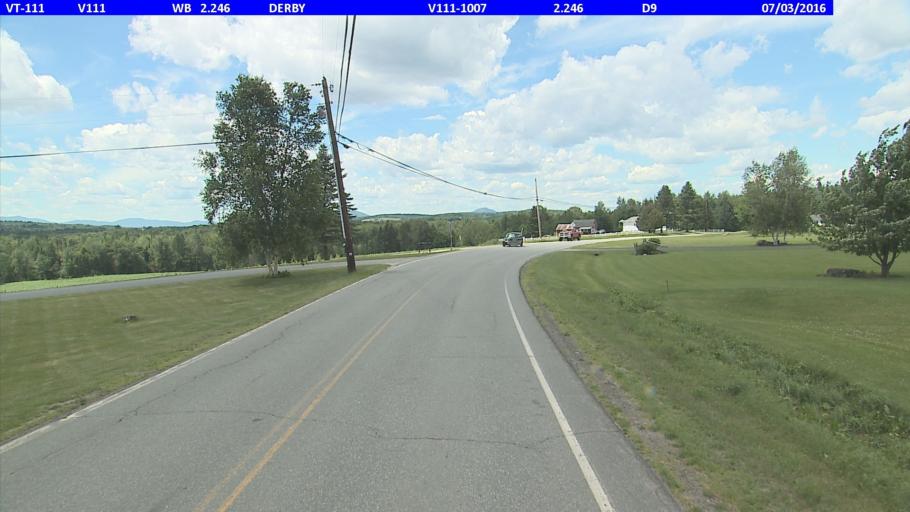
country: US
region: Vermont
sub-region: Orleans County
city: Newport
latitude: 44.9396
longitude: -72.0945
